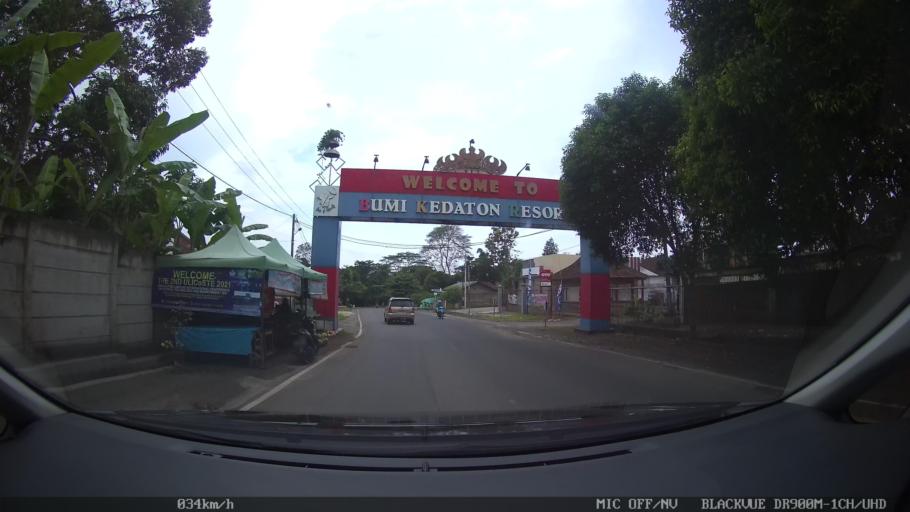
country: ID
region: Lampung
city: Bandarlampung
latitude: -5.4358
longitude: 105.2227
